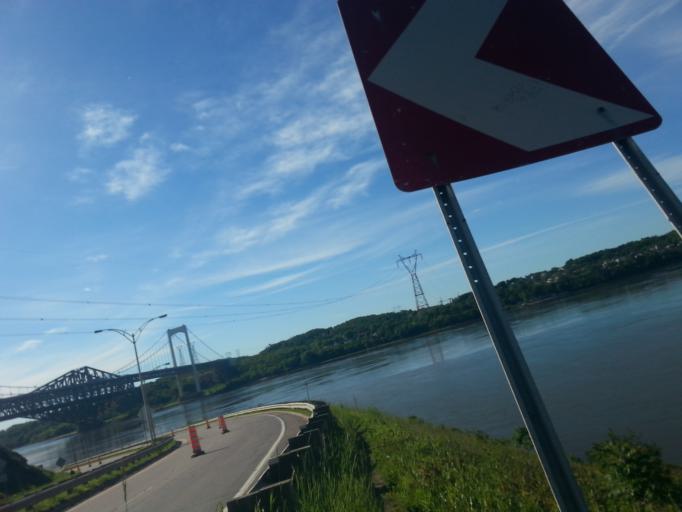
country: CA
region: Quebec
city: L'Ancienne-Lorette
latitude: 46.7493
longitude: -71.2987
